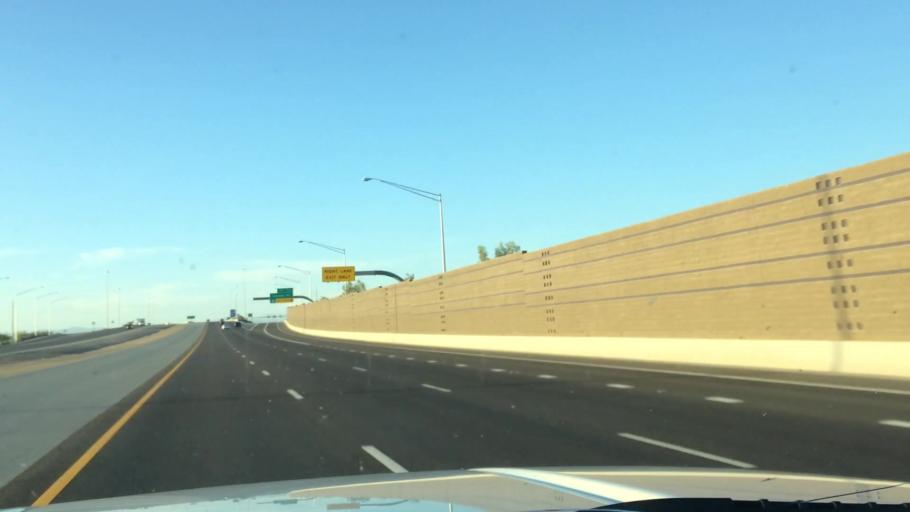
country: US
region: Arizona
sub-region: Maricopa County
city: Citrus Park
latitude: 33.5890
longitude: -112.4179
